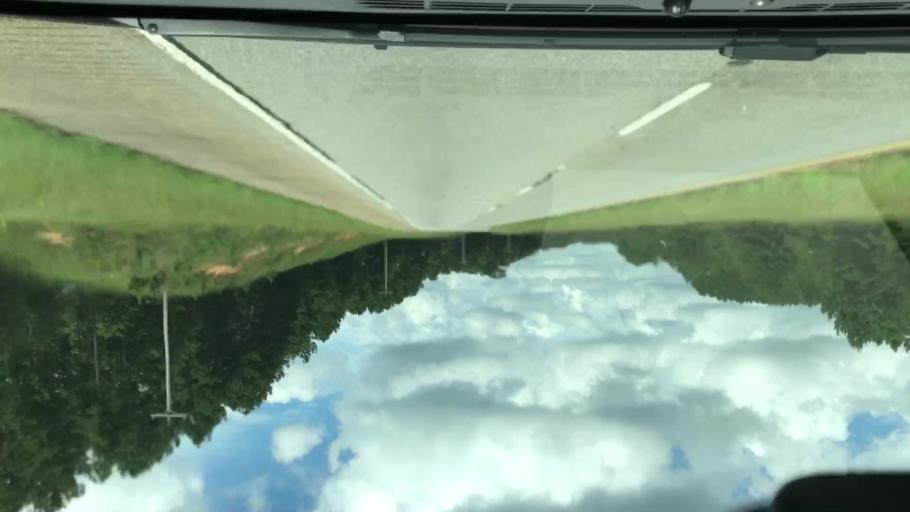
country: US
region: Georgia
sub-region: Stewart County
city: Lumpkin
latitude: 32.1128
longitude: -84.8140
